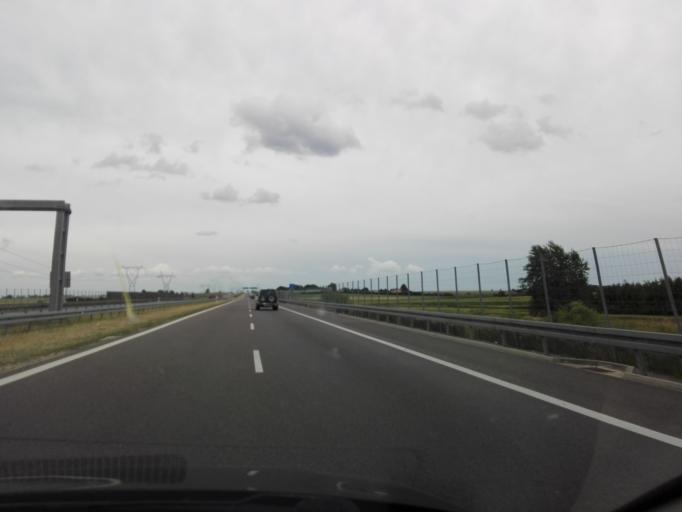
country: PL
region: Lublin Voivodeship
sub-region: Powiat pulawski
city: Markuszow
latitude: 51.3838
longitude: 22.2741
